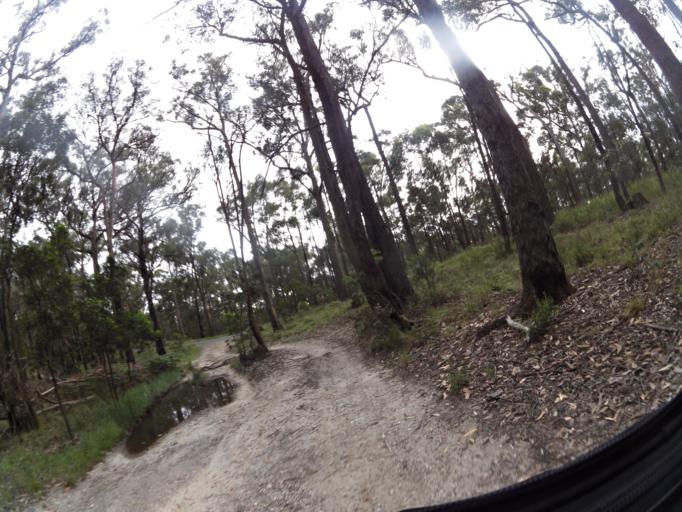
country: AU
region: Victoria
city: Brown Hill
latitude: -37.5227
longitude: 143.9073
